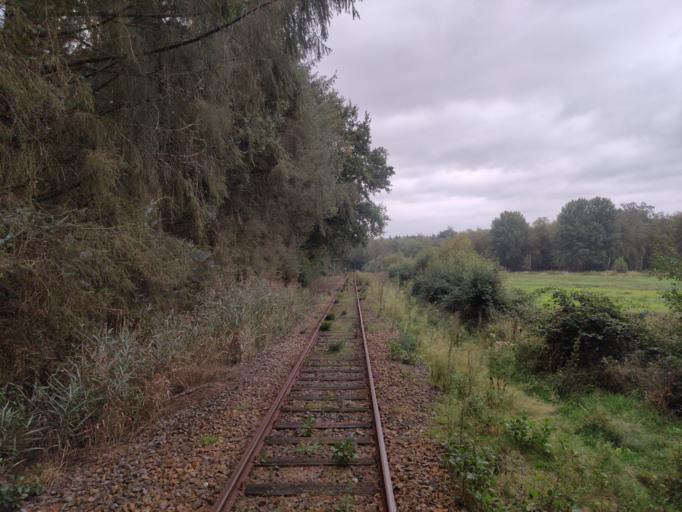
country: DE
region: Lower Saxony
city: Basdahl
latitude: 53.4196
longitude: 9.0162
